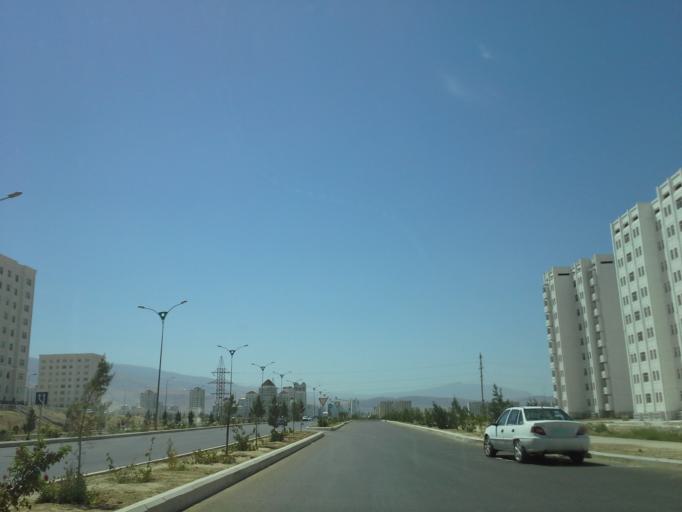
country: TM
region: Ahal
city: Ashgabat
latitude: 37.8954
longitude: 58.4083
